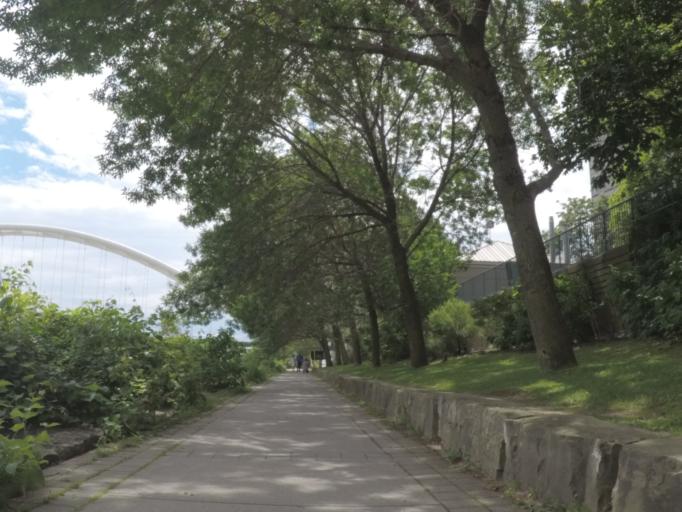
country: CA
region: Ontario
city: Toronto
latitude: 43.6322
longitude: -79.4728
